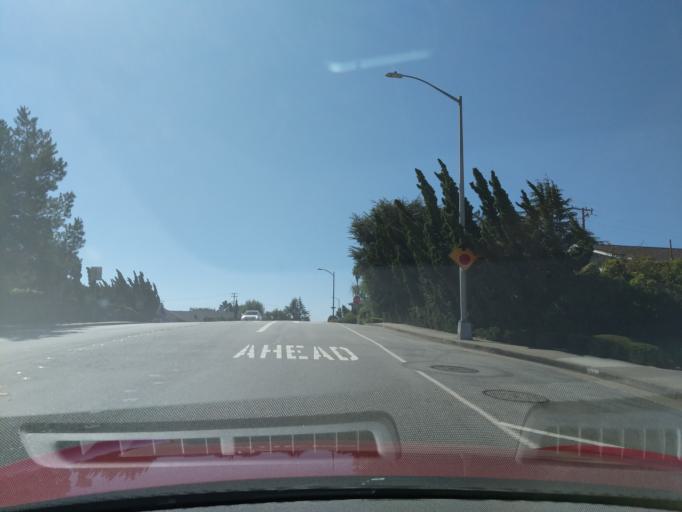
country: US
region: California
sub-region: San Mateo County
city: Highlands-Baywood Park
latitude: 37.5326
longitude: -122.3243
